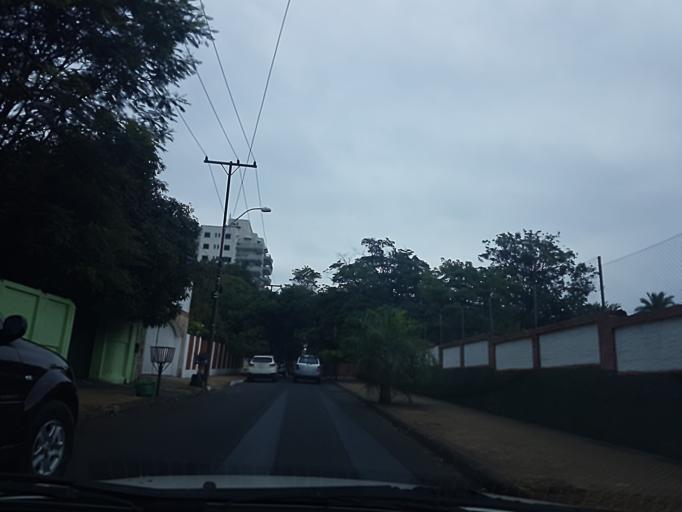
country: PY
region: Asuncion
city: Asuncion
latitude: -25.2892
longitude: -57.6143
